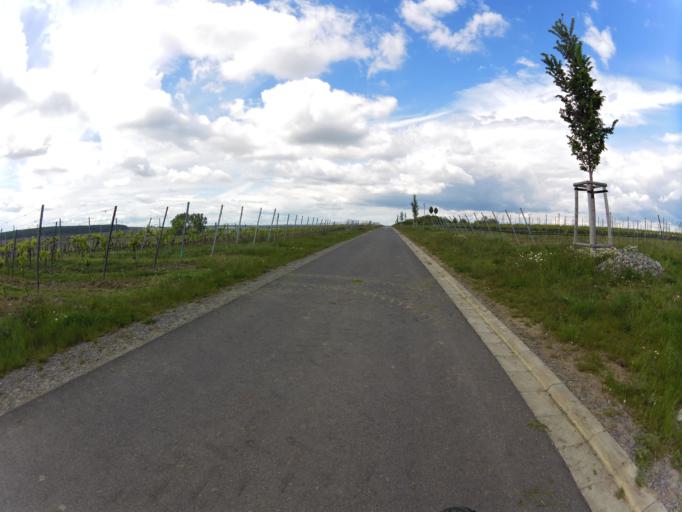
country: DE
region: Bavaria
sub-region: Regierungsbezirk Unterfranken
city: Sommerach
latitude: 49.8433
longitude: 10.1948
